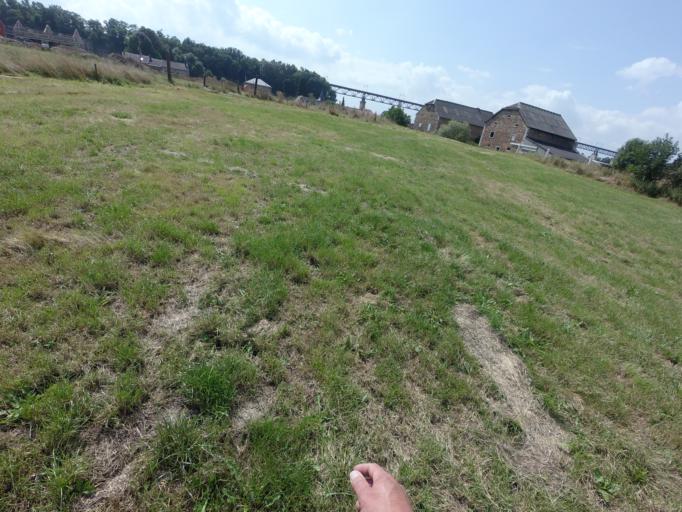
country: BE
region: Wallonia
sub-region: Province de Liege
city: La Calamine
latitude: 50.7231
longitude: 5.9915
